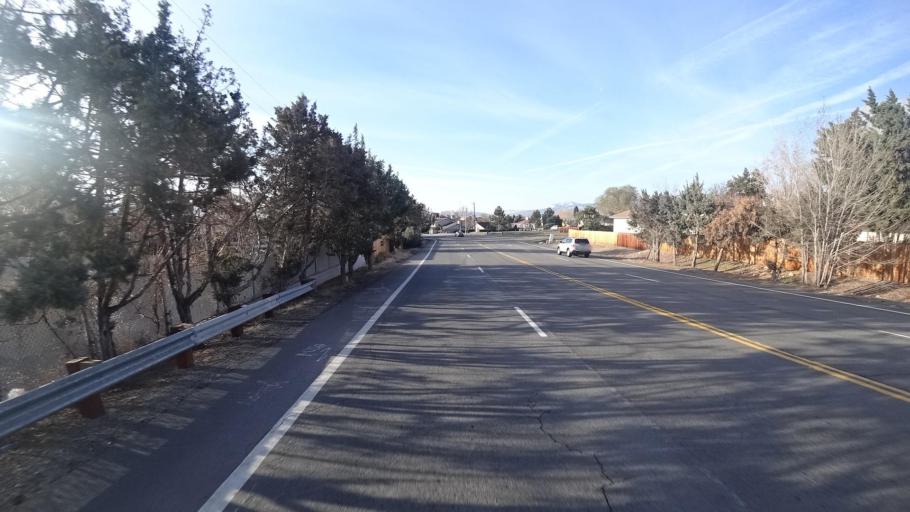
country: US
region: Nevada
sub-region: Washoe County
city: Sparks
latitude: 39.5545
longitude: -119.7791
